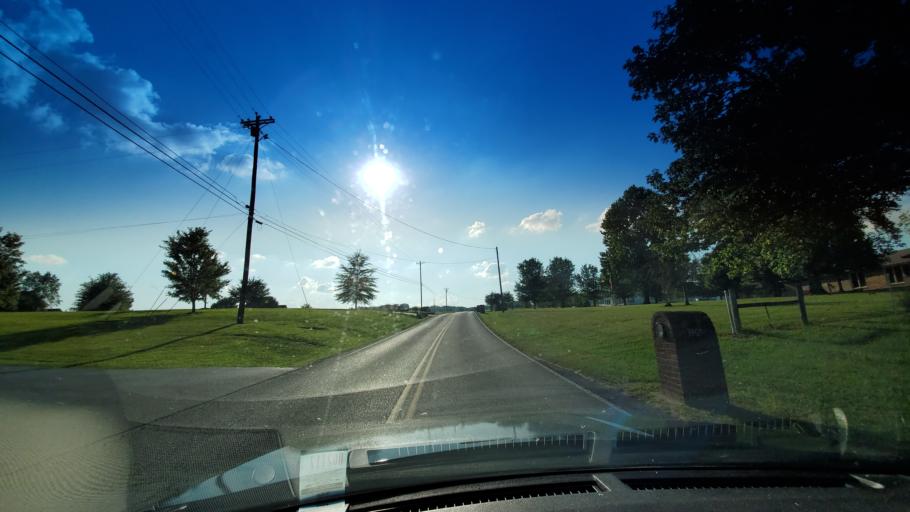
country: US
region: Tennessee
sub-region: Wilson County
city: Lebanon
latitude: 36.1678
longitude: -86.3631
